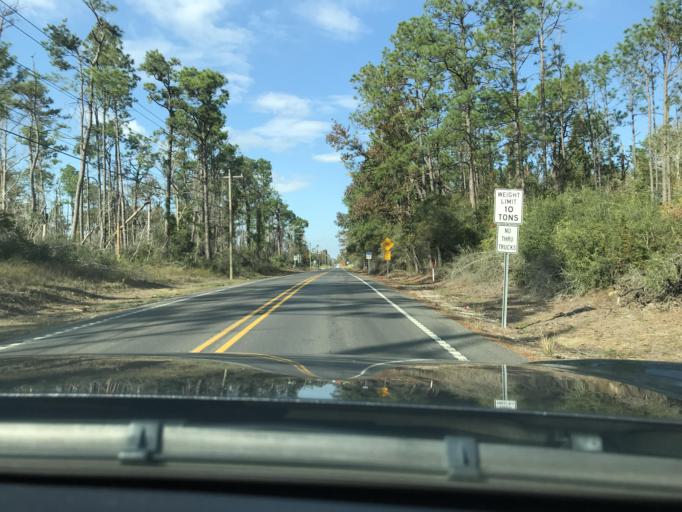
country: US
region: Louisiana
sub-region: Calcasieu Parish
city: Westlake
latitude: 30.3057
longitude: -93.2584
